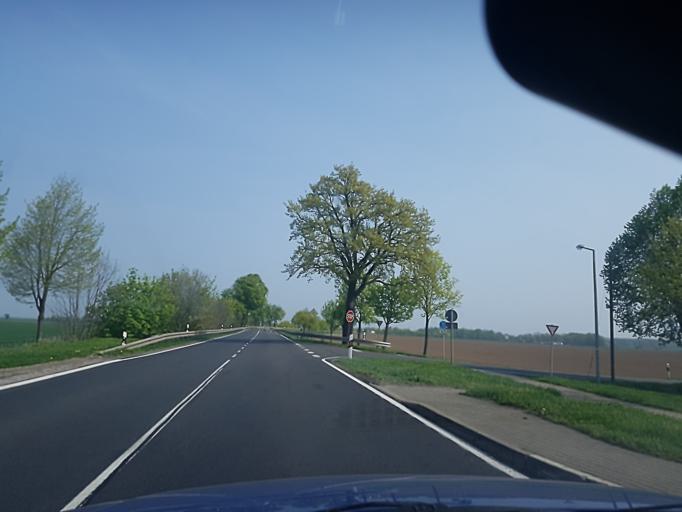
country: DE
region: Saxony
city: Torgau
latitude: 51.5717
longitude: 13.0274
